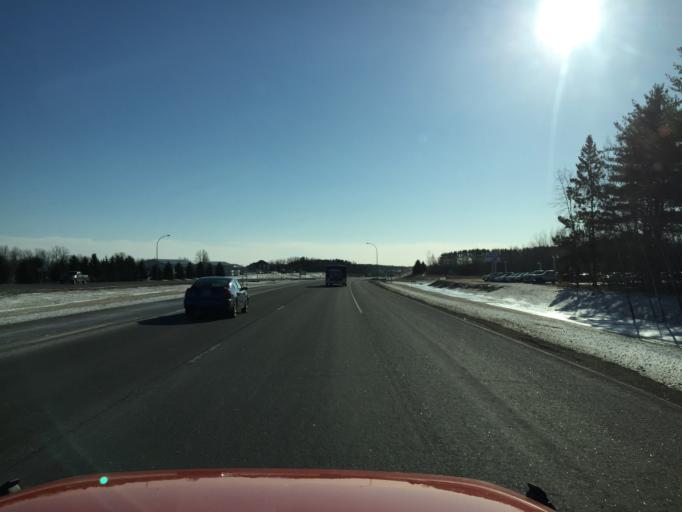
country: US
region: Minnesota
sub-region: Mille Lacs County
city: Milaca
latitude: 45.7859
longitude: -93.6520
